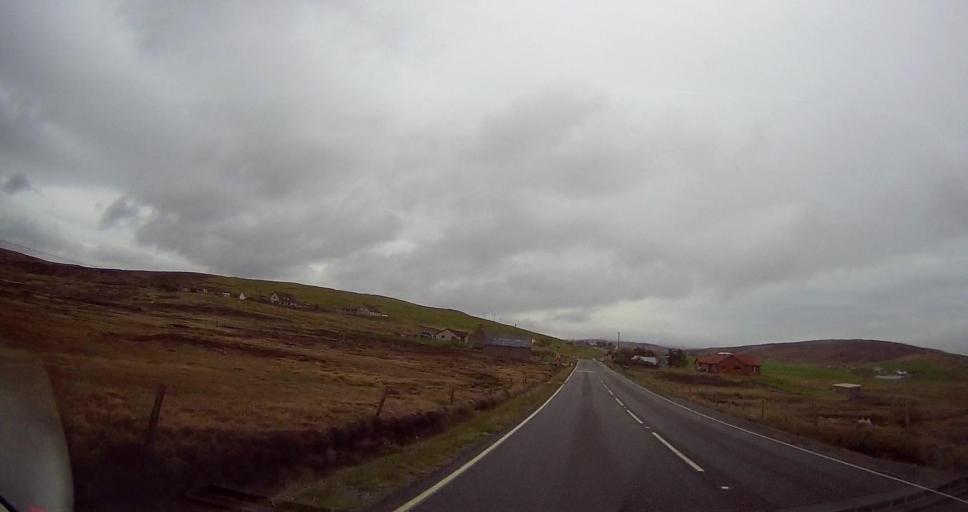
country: GB
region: Scotland
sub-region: Shetland Islands
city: Lerwick
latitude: 60.2333
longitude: -1.2347
